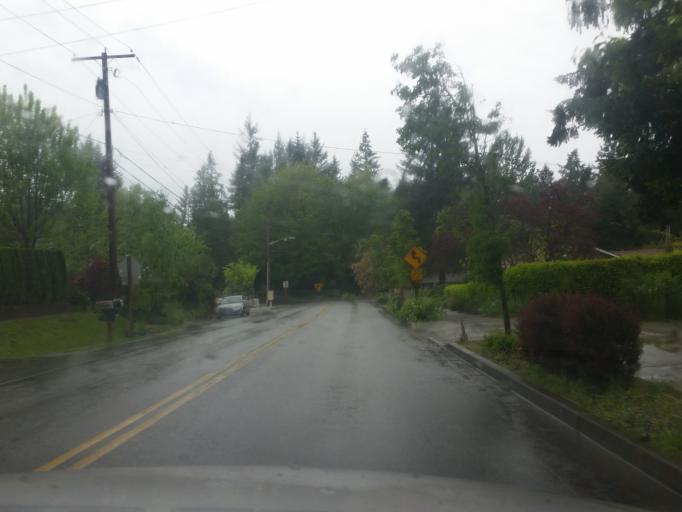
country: US
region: Washington
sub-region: King County
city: Kenmore
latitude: 47.7406
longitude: -122.2340
